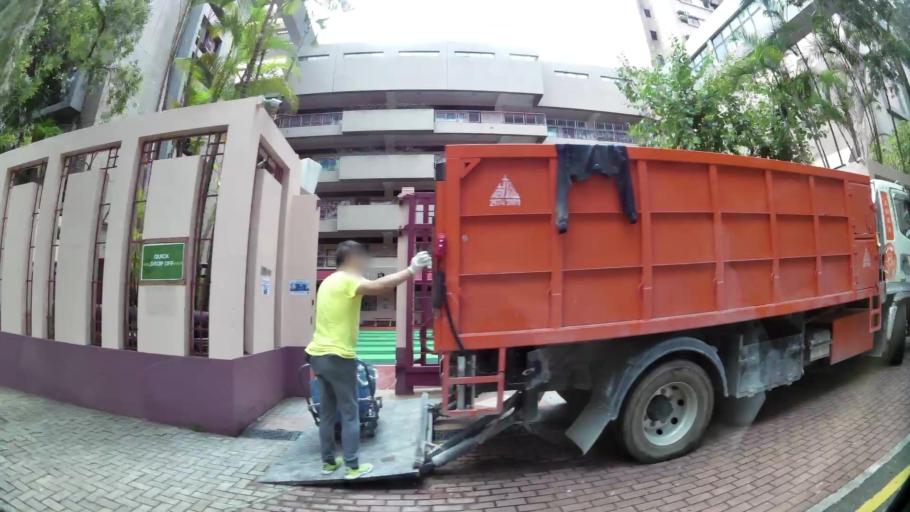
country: HK
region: Wanchai
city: Wan Chai
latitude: 22.2839
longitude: 114.1981
